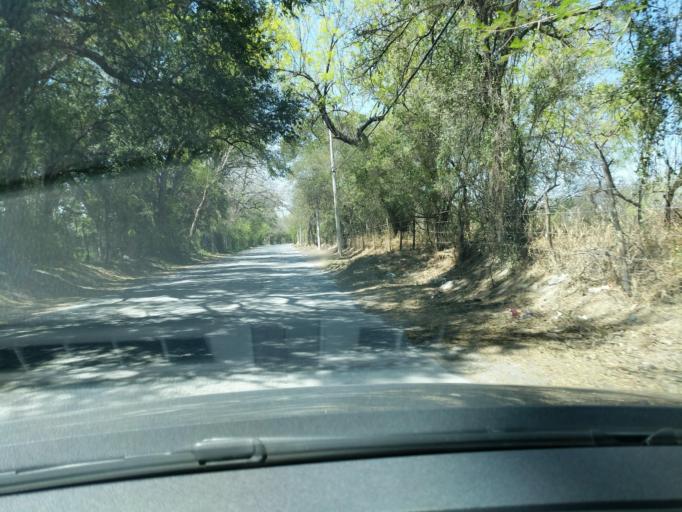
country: MX
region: Nuevo Leon
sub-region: Pesqueria
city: Colinas del Aeropuerto
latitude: 25.8127
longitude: -100.1224
